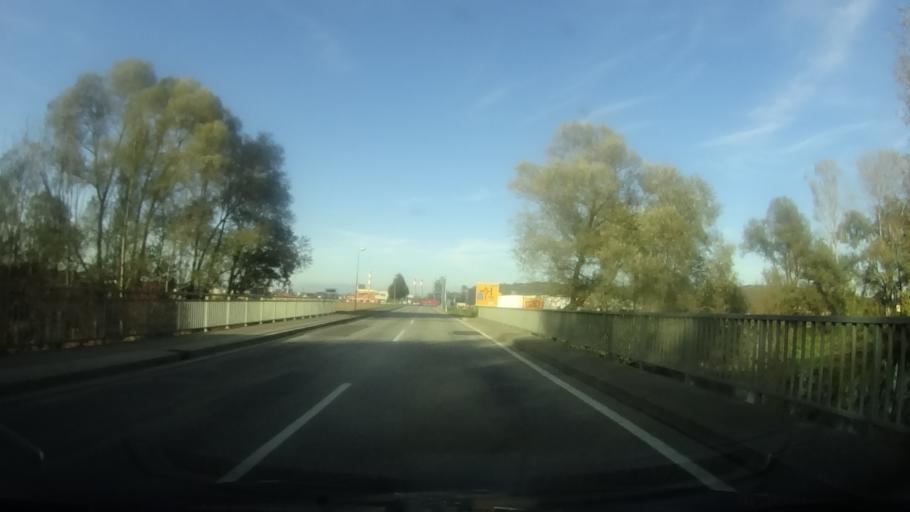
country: AT
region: Styria
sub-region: Politischer Bezirk Leibnitz
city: Weitendorf
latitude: 46.8844
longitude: 15.4891
